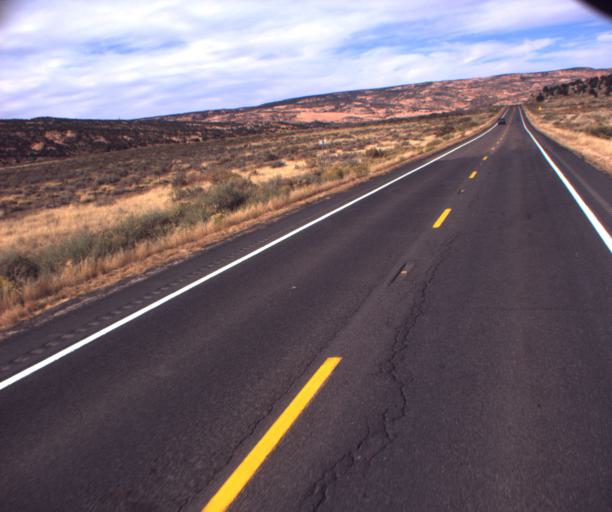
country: US
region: Arizona
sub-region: Navajo County
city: Kayenta
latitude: 36.5880
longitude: -110.4719
